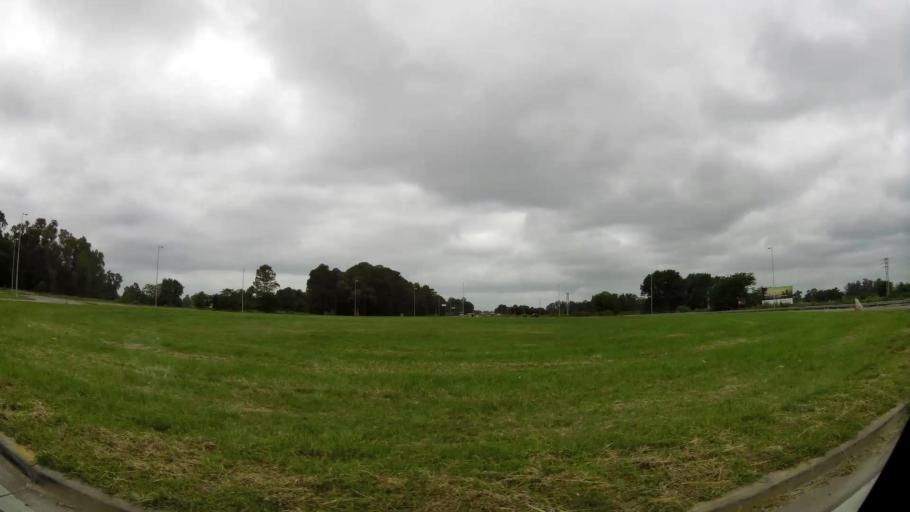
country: AR
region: Buenos Aires
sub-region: Partido de San Vicente
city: San Vicente
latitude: -35.0555
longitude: -58.4427
